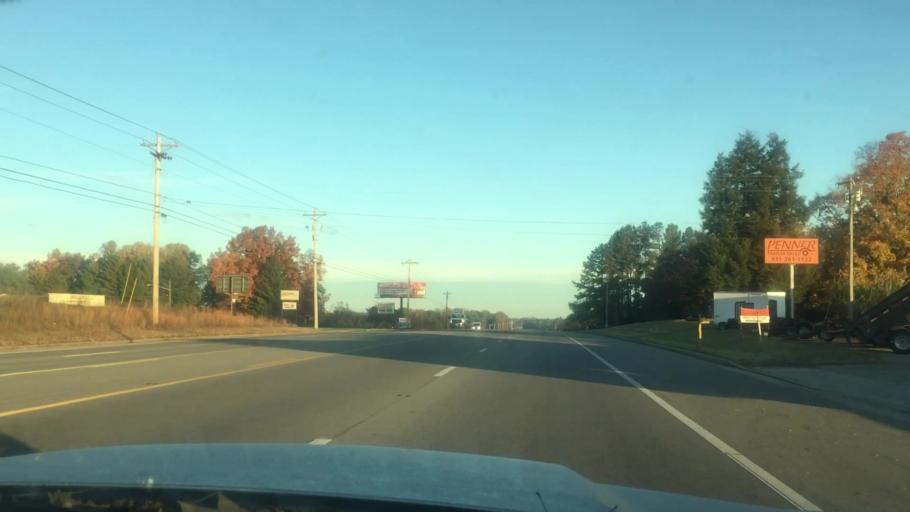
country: US
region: Tennessee
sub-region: Franklin County
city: Decherd
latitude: 35.2252
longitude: -86.1047
